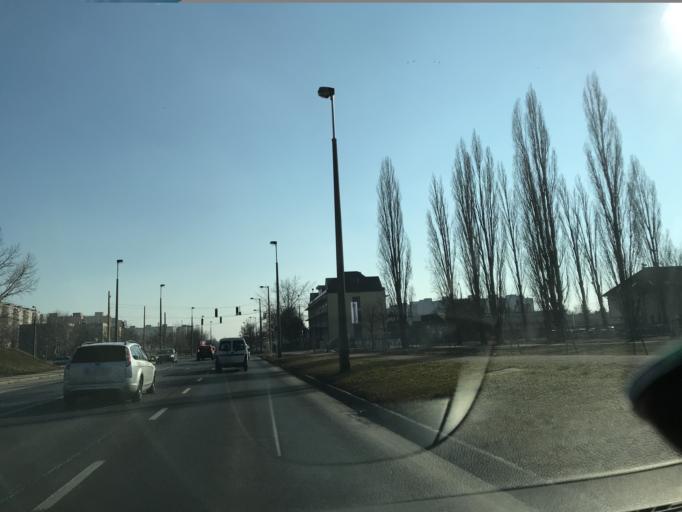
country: HU
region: Gyor-Moson-Sopron
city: Gyor
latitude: 47.6715
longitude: 17.6341
